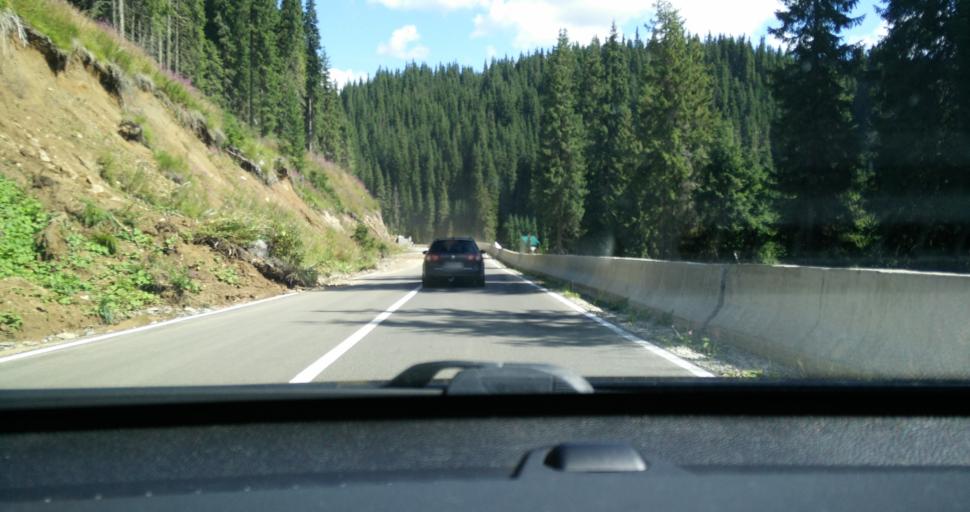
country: RO
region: Hunedoara
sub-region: Oras Petrila
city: Petrila
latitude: 45.5066
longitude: 23.6491
